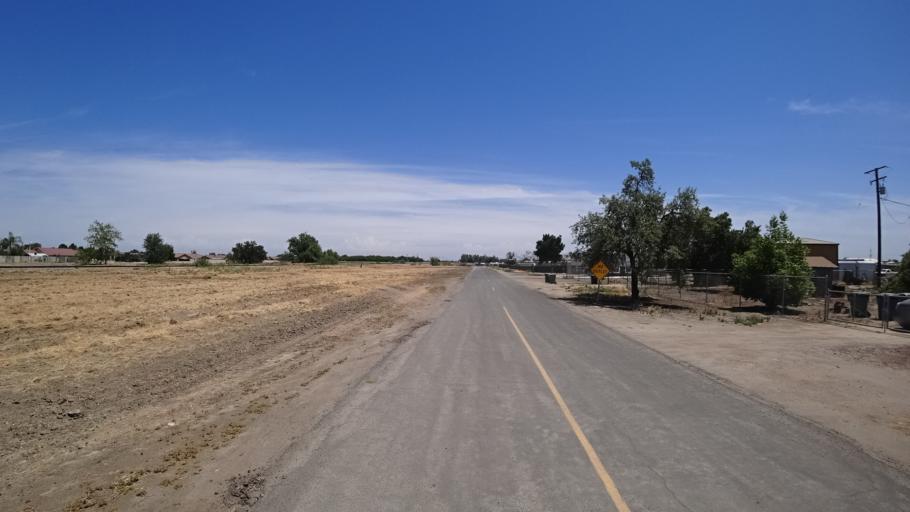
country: US
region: California
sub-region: Kings County
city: Armona
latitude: 36.3160
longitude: -119.7016
